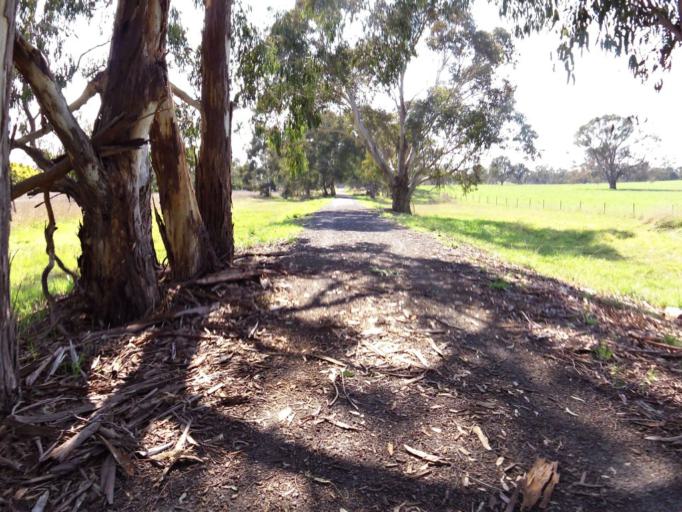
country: AU
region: Victoria
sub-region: Murrindindi
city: Alexandra
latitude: -37.1230
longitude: 145.6006
